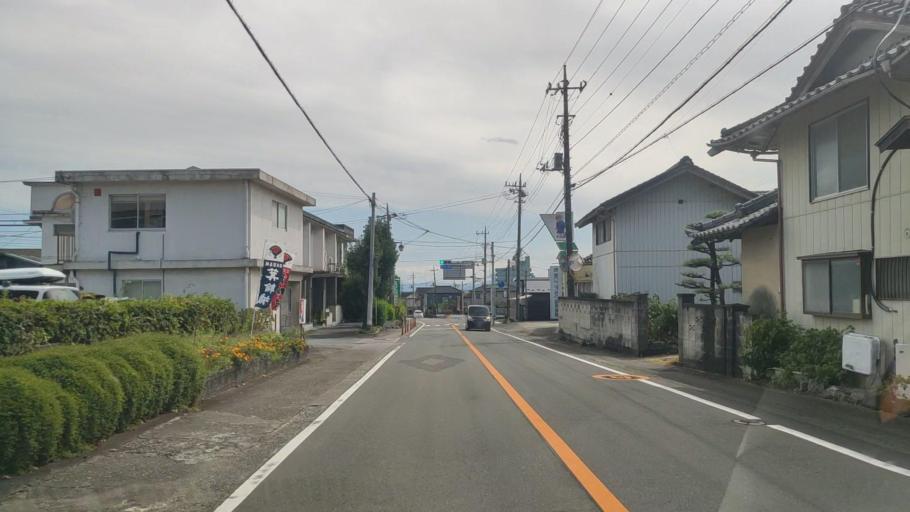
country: JP
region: Gunma
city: Kanekomachi
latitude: 36.3892
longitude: 138.9584
